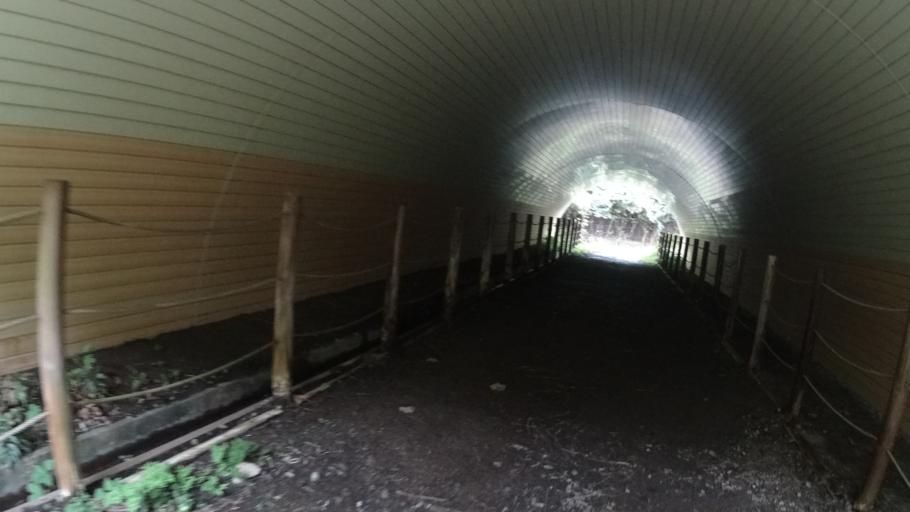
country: JP
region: Kanagawa
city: Zushi
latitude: 35.3511
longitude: 139.5947
